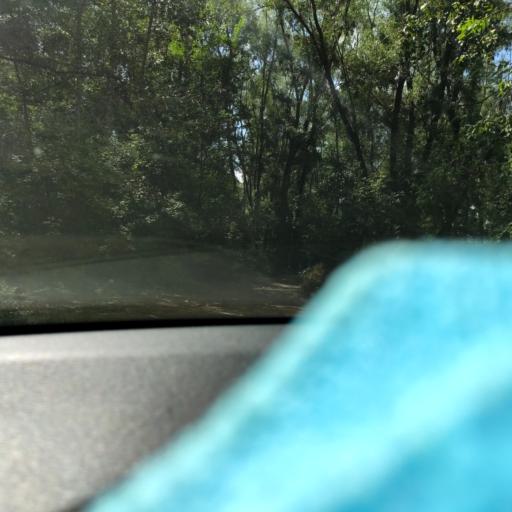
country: RU
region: Samara
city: Smyshlyayevka
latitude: 53.2202
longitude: 50.3440
